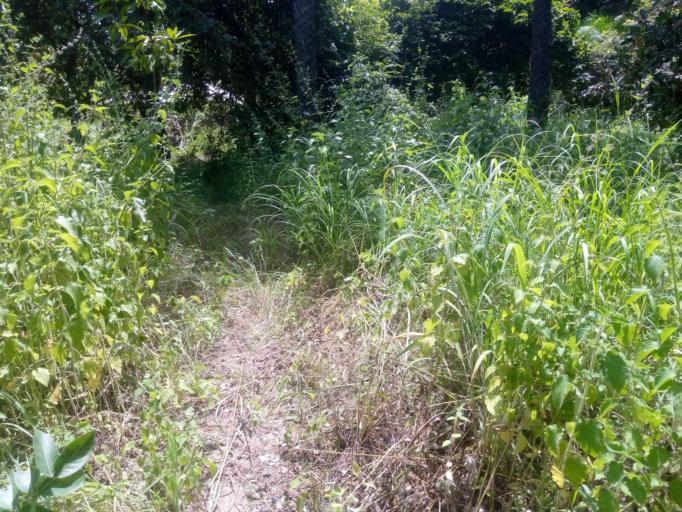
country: GM
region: Western
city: Gunjur
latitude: 13.0397
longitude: -16.7281
